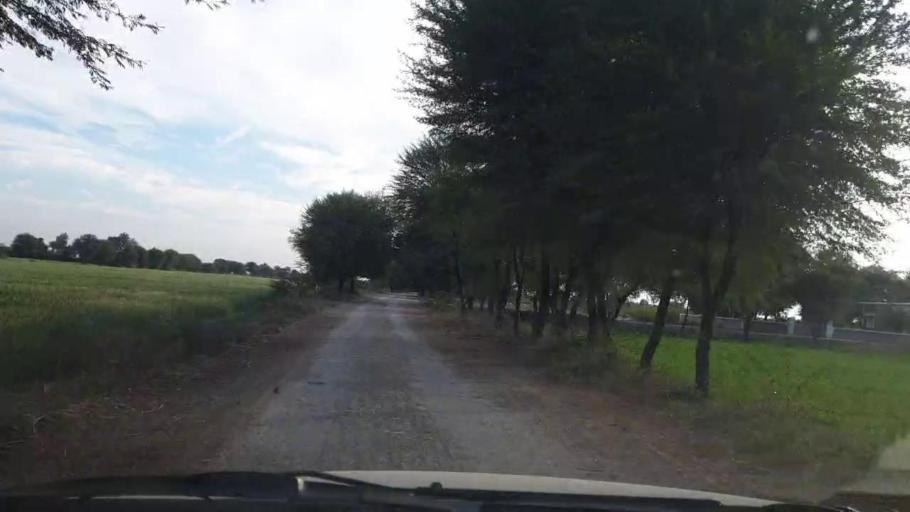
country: PK
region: Sindh
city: Pithoro
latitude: 25.6472
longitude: 69.2764
